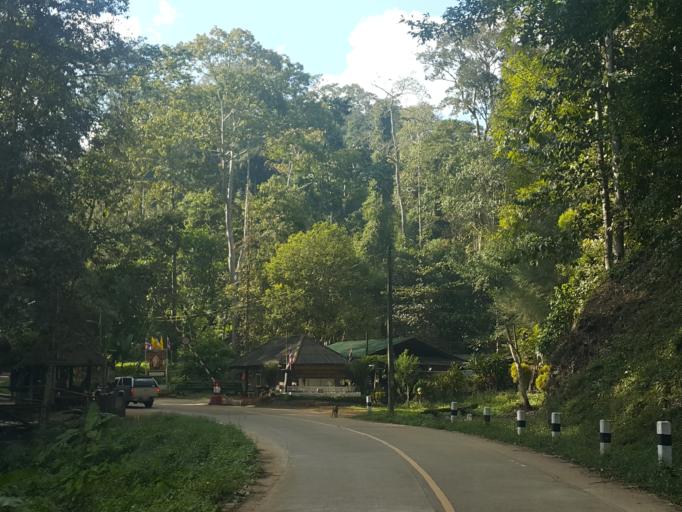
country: TH
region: Chiang Mai
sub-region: Amphoe Chiang Dao
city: Chiang Dao
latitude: 19.4139
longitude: 98.9156
